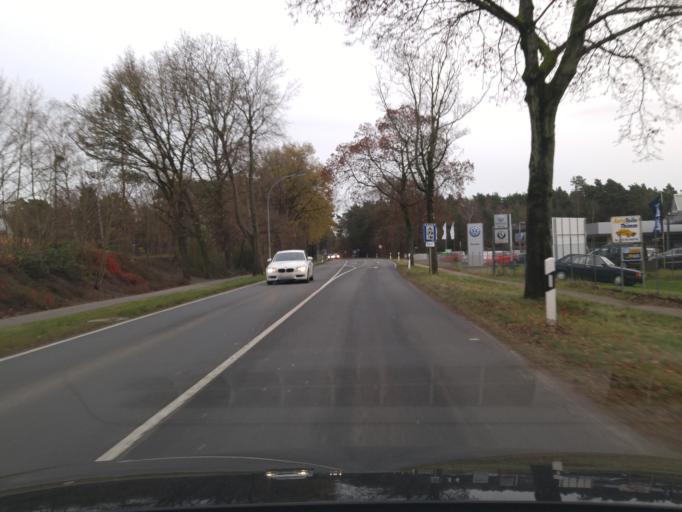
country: DE
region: Lower Saxony
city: Winsen
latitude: 52.6754
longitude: 9.9273
